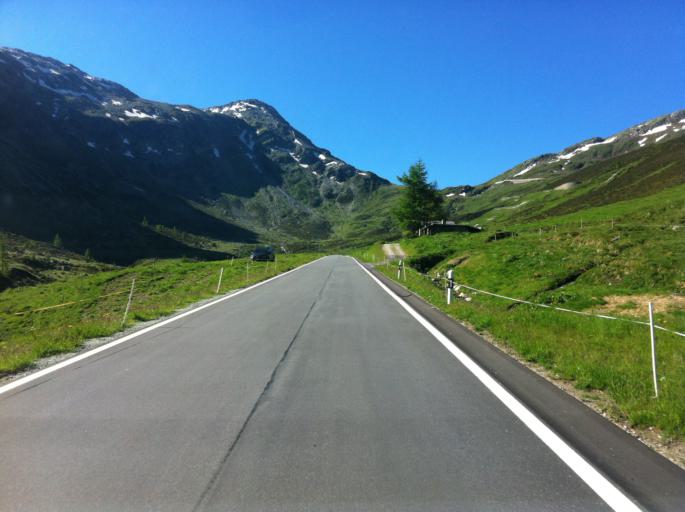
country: CH
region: Grisons
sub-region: Hinterrhein District
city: Hinterrhein
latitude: 46.5334
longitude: 9.3267
